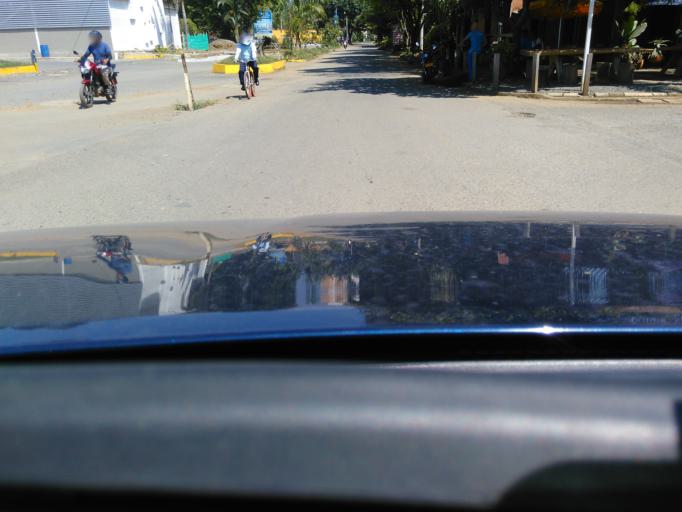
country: CO
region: Valle del Cauca
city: Jamundi
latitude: 3.2485
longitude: -76.5485
